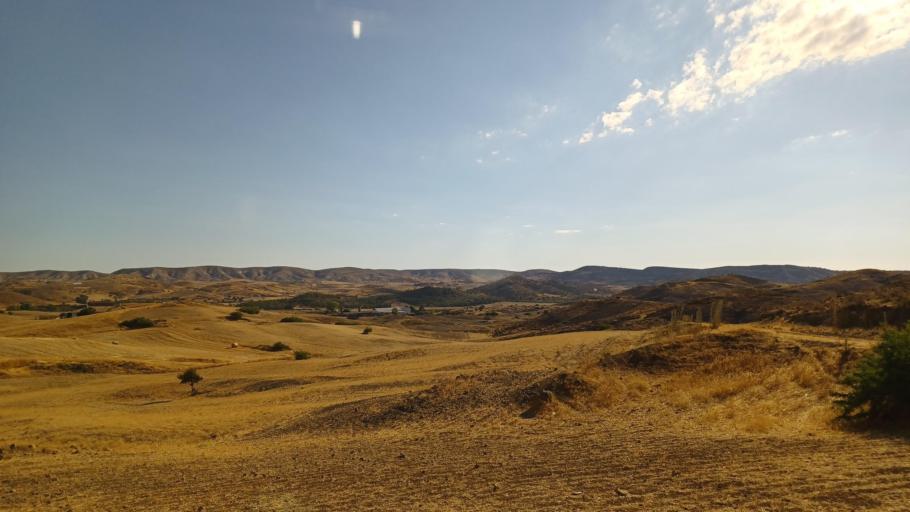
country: CY
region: Larnaka
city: Troulloi
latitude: 35.0053
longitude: 33.6165
